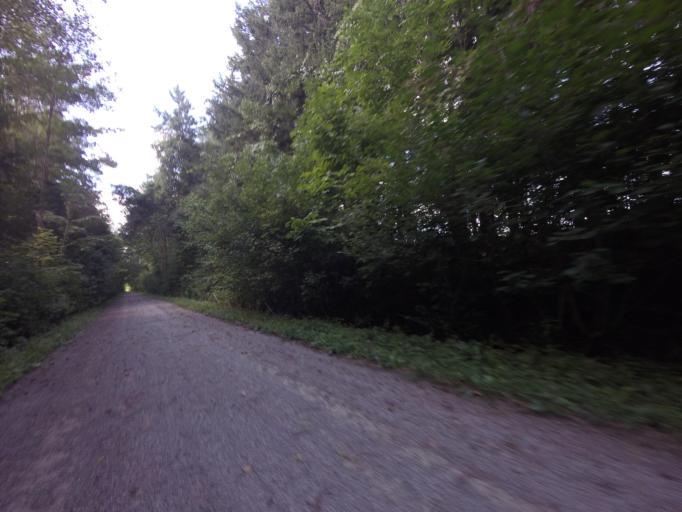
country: CA
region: Ontario
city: Huron East
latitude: 43.6728
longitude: -81.2816
